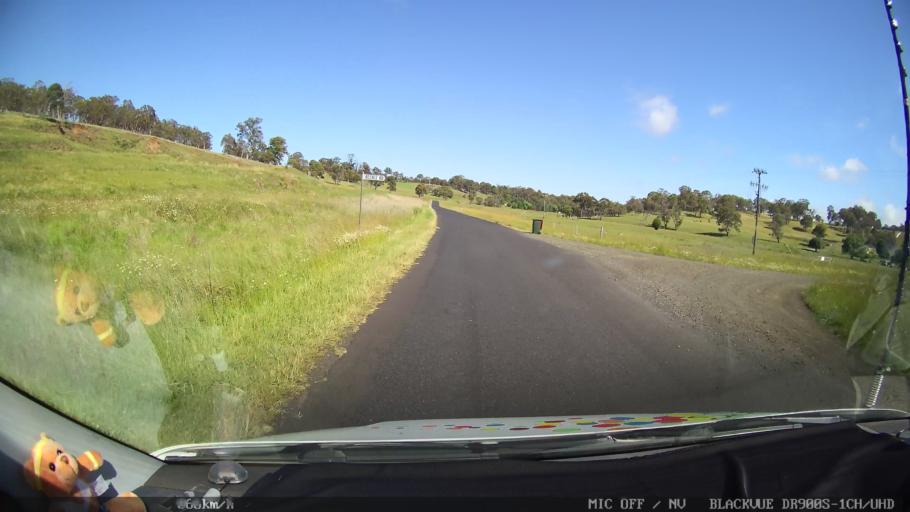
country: AU
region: New South Wales
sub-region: Guyra
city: Guyra
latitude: -30.1176
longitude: 151.6875
